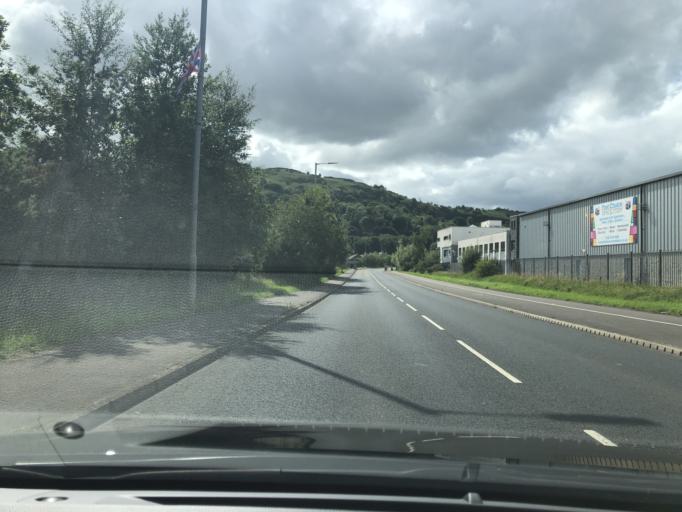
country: GB
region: Northern Ireland
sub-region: Ards District
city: Newtownards
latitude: 54.5832
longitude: -5.7032
